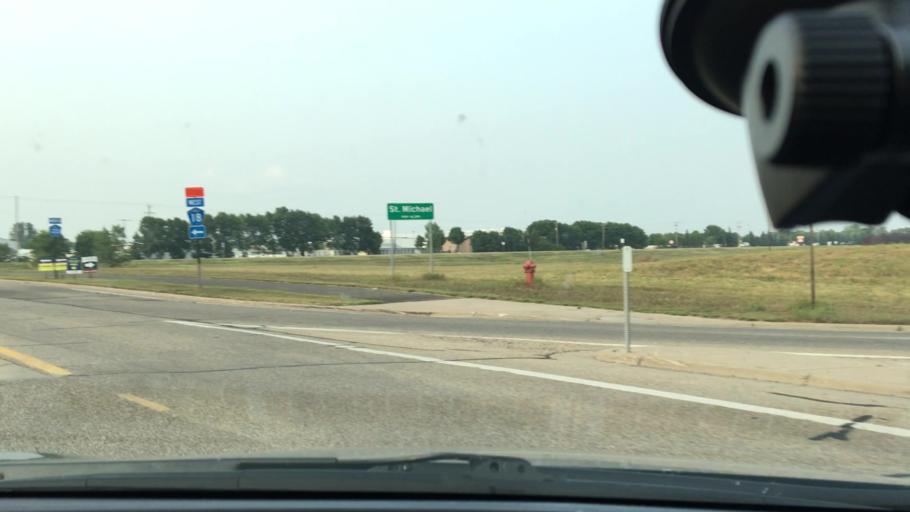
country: US
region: Minnesota
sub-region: Wright County
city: Albertville
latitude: 45.2110
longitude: -93.6241
